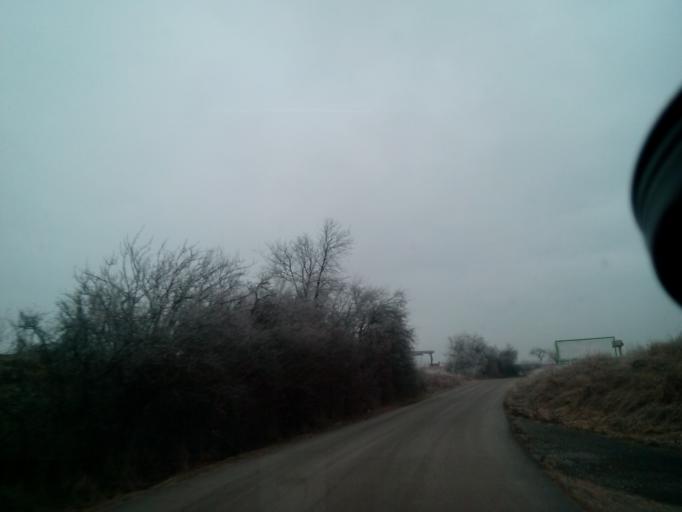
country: SK
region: Presovsky
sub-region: Okres Poprad
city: Poprad
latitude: 48.9665
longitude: 20.3857
